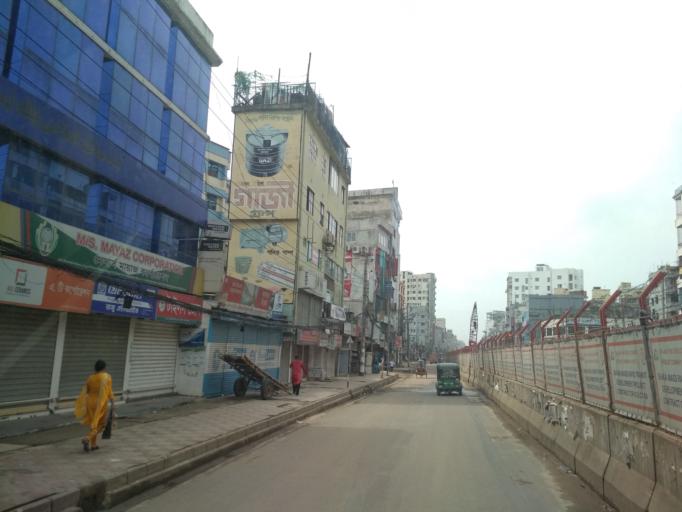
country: BD
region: Dhaka
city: Azimpur
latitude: 23.8054
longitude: 90.3694
